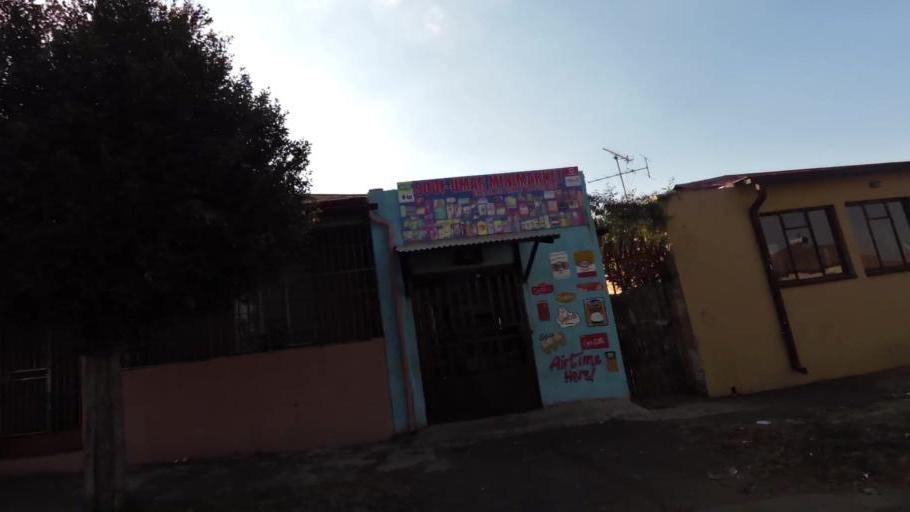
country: ZA
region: Gauteng
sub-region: City of Johannesburg Metropolitan Municipality
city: Johannesburg
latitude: -26.1923
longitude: 28.0163
